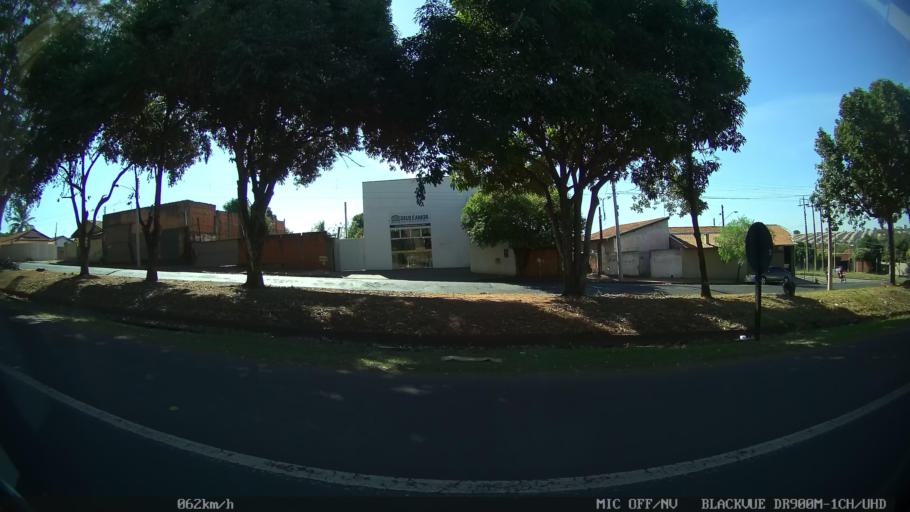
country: BR
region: Sao Paulo
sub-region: Olimpia
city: Olimpia
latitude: -20.7380
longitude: -48.8883
